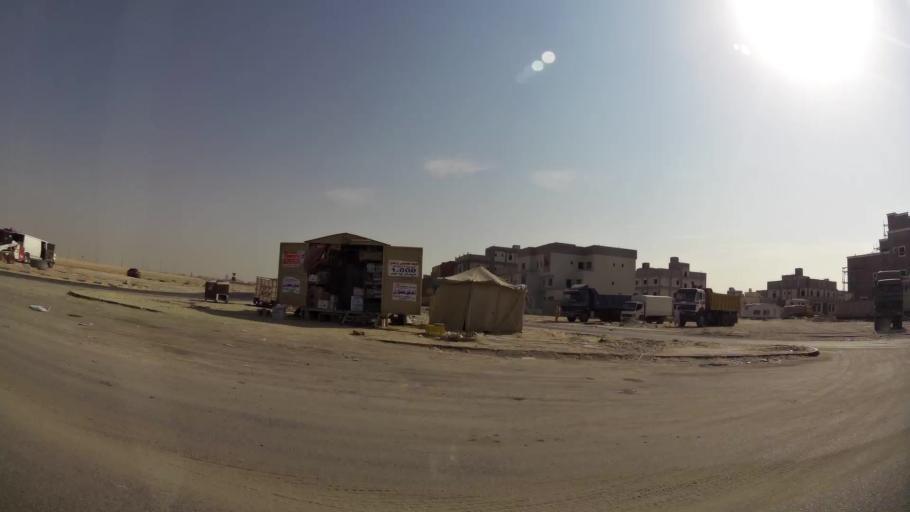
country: KW
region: Al Ahmadi
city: Al Wafrah
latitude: 28.7803
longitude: 48.0694
